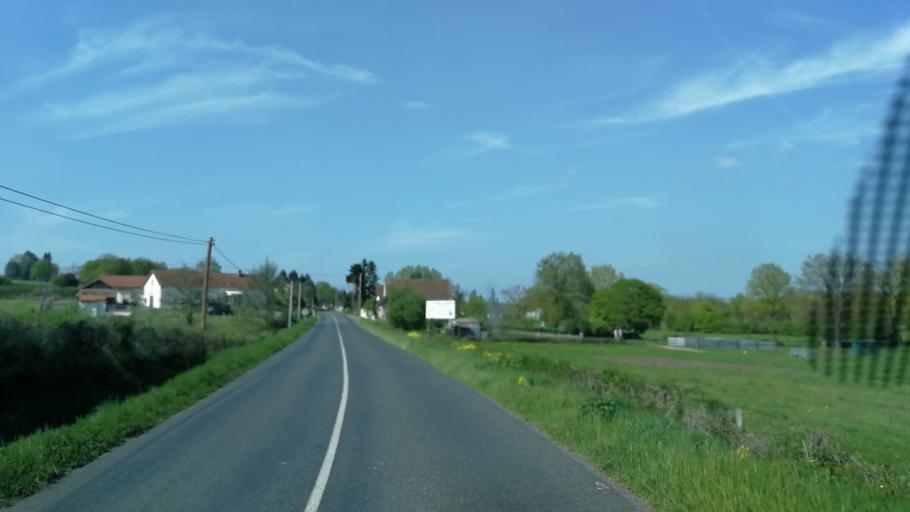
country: FR
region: Auvergne
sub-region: Departement de l'Allier
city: Saint-Gerand-le-Puy
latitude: 46.3691
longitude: 3.5806
